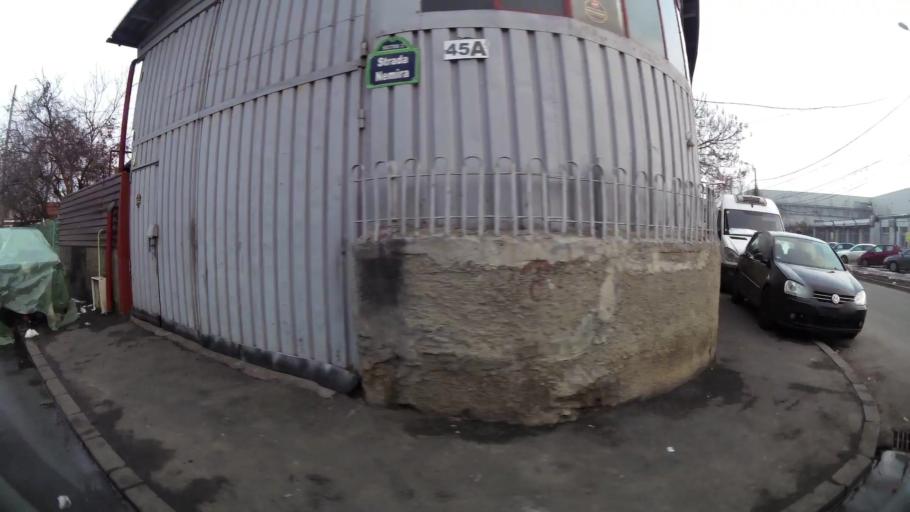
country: RO
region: Ilfov
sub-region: Comuna Fundeni-Dobroesti
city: Fundeni
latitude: 44.4703
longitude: 26.1643
